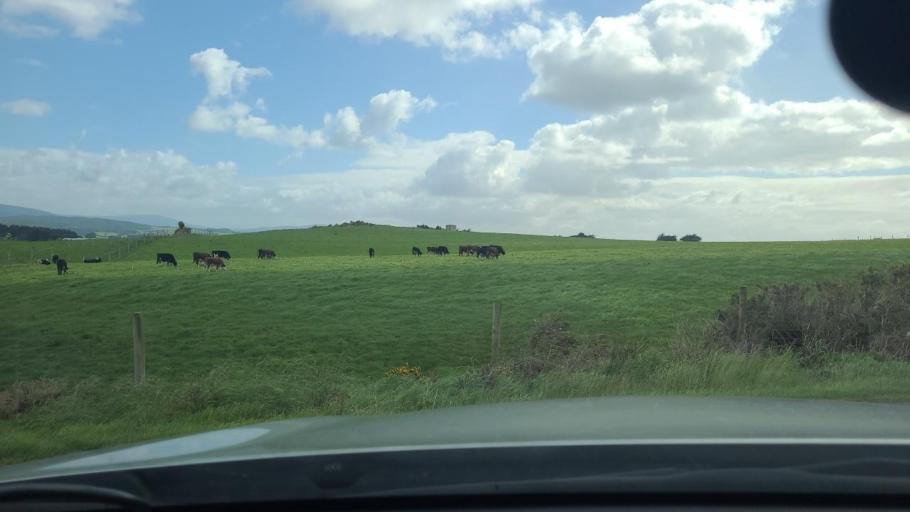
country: NZ
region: Southland
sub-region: Southland District
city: Riverton
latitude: -46.3524
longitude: 167.9505
